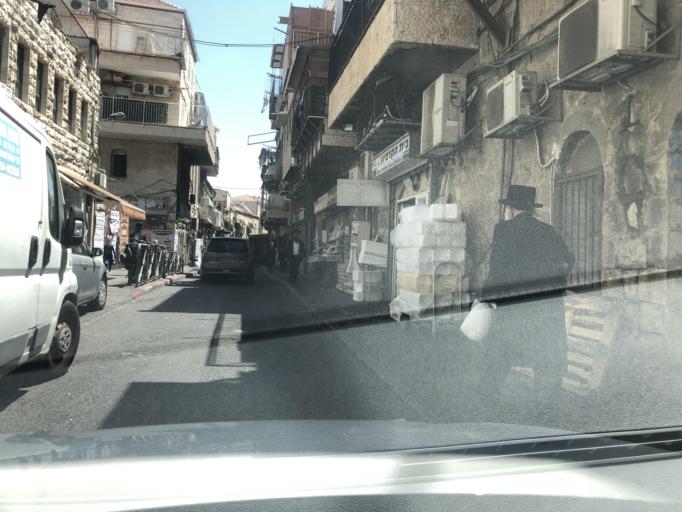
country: IL
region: Jerusalem
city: West Jerusalem
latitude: 31.7876
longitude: 35.2219
